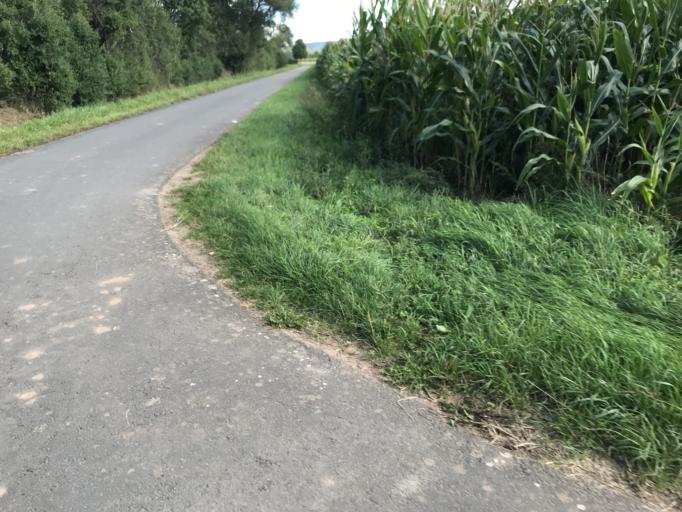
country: DE
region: Hesse
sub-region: Regierungsbezirk Kassel
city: Eschwege
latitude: 51.2036
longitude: 10.0390
